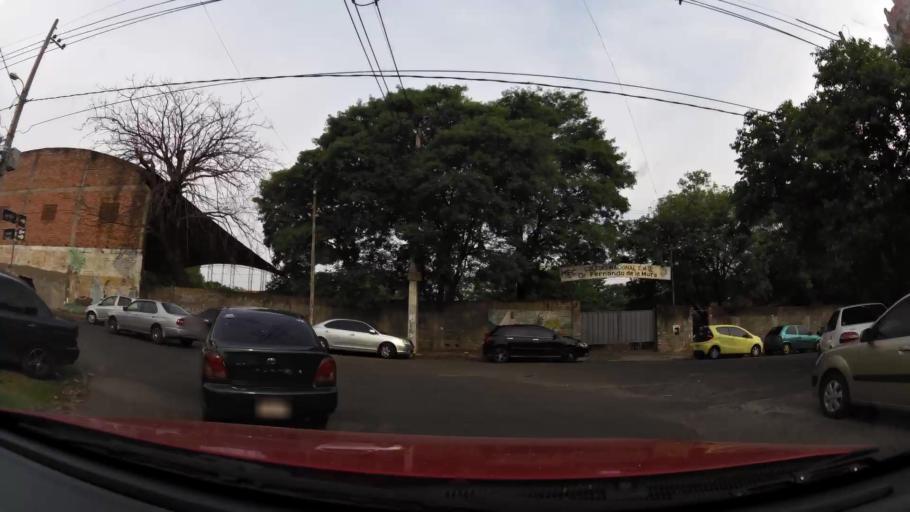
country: PY
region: Asuncion
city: Asuncion
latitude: -25.3046
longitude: -57.6173
